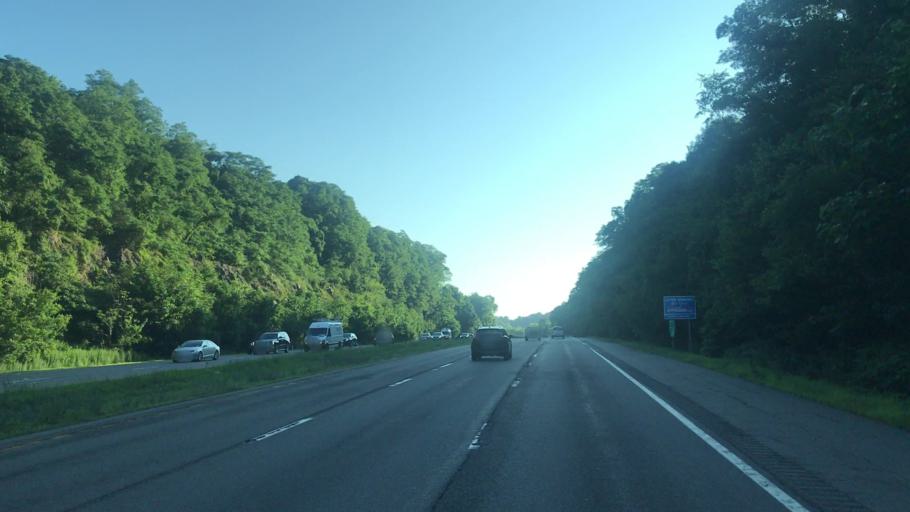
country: US
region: New York
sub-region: Westchester County
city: Purchase
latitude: 41.0625
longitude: -73.7250
